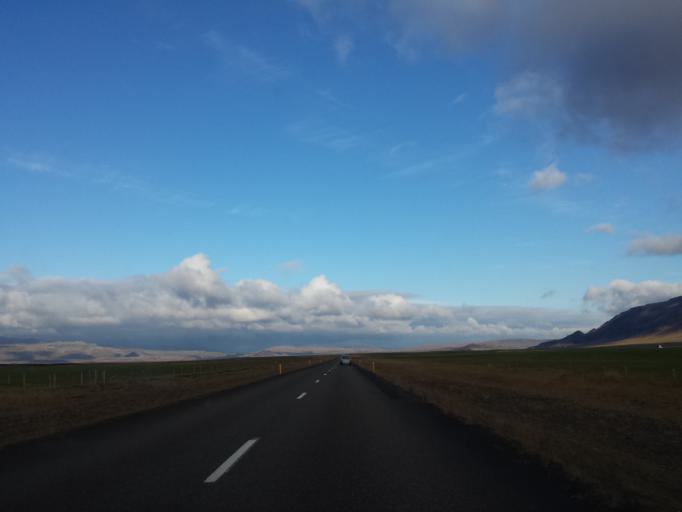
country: IS
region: West
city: Borgarnes
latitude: 64.7713
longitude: -22.2669
